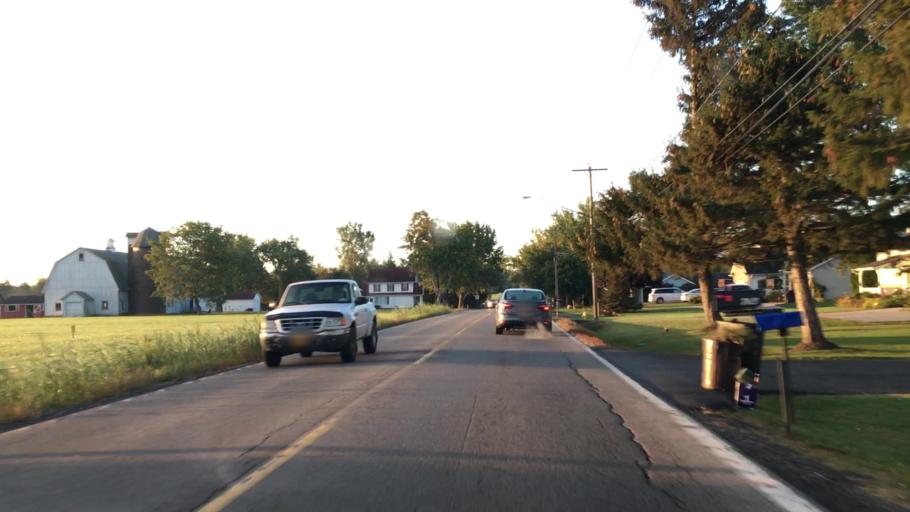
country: US
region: New York
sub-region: Erie County
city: Lancaster
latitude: 42.8660
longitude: -78.6763
